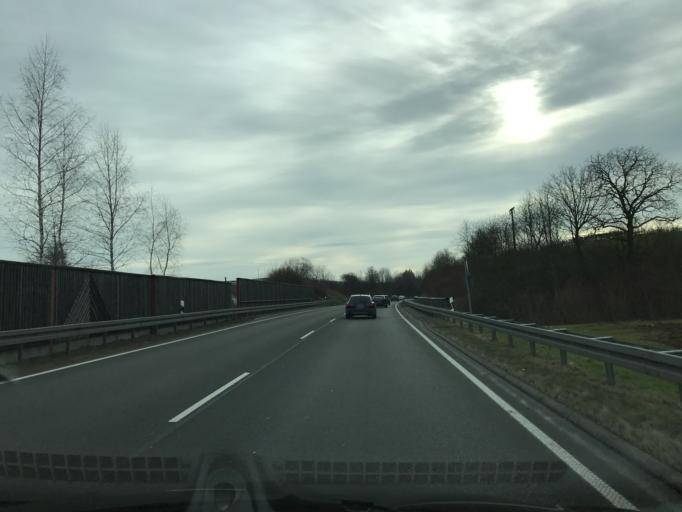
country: DE
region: Baden-Wuerttemberg
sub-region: Tuebingen Region
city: Kressbronn am Bodensee
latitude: 47.6039
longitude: 9.6218
